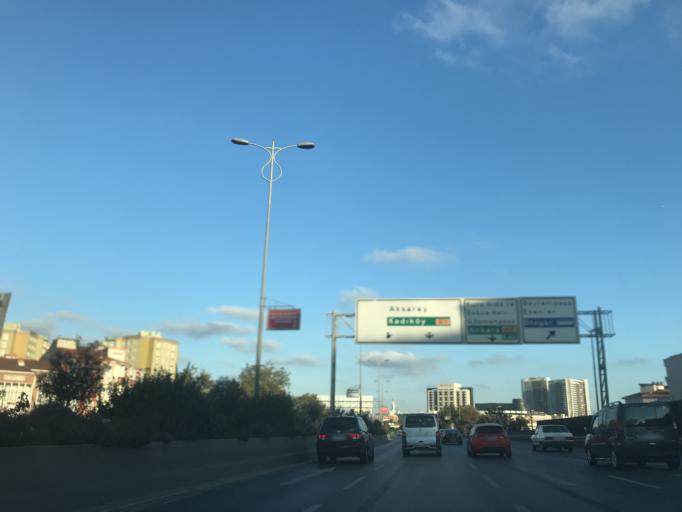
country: TR
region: Istanbul
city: Esenler
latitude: 41.0468
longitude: 28.8794
